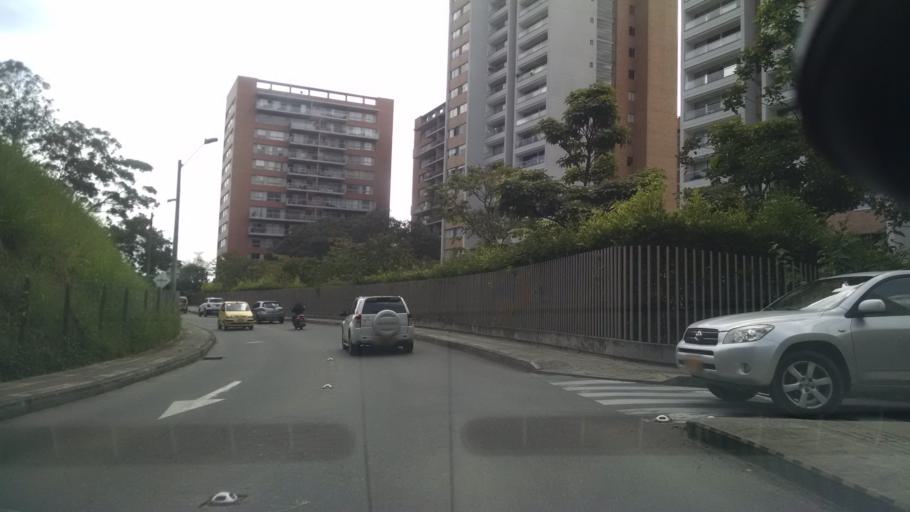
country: CO
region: Antioquia
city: Envigado
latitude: 6.1957
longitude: -75.5704
